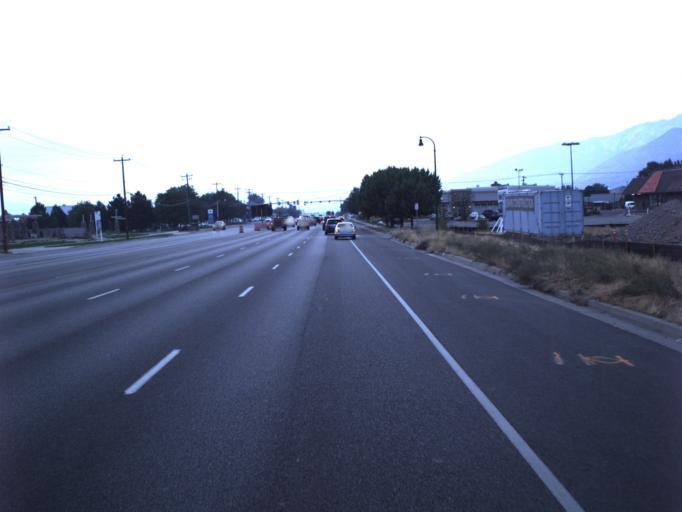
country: US
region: Utah
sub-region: Utah County
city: Lindon
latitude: 40.3312
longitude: -111.7113
